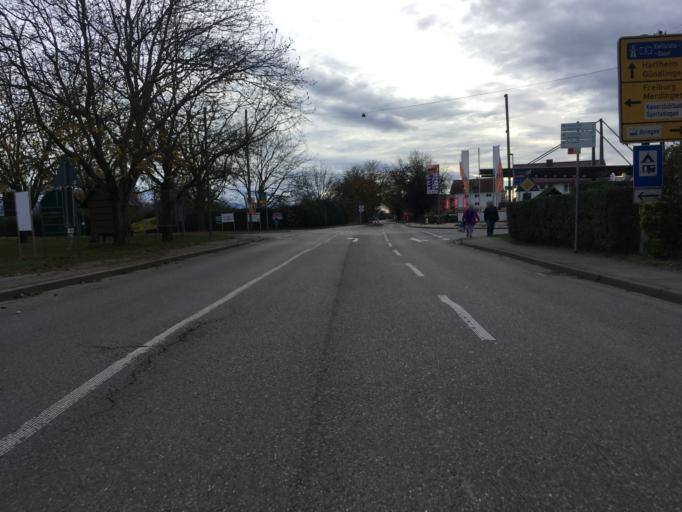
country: DE
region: Baden-Wuerttemberg
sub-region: Freiburg Region
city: Ihringen
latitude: 48.0380
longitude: 7.6478
